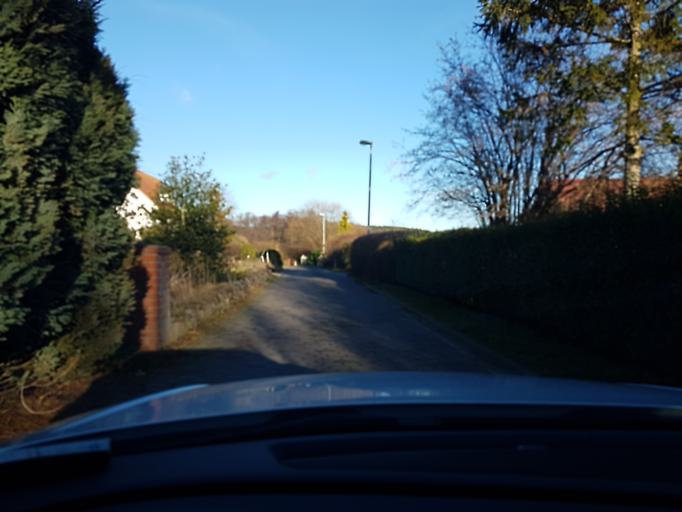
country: DE
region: Mecklenburg-Vorpommern
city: Ostseebad Sellin
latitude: 54.3680
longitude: 13.6754
